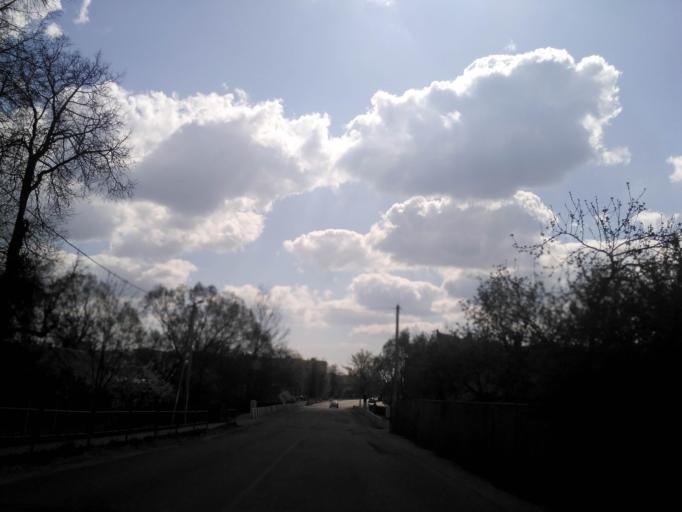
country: BY
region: Minsk
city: Radashkovichy
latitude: 54.1579
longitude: 27.2396
